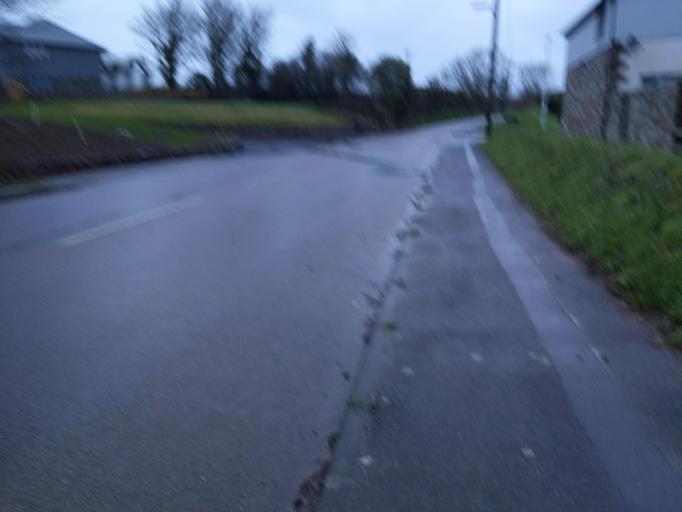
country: GB
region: England
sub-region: Devon
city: Wembury
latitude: 50.3197
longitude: -4.0348
